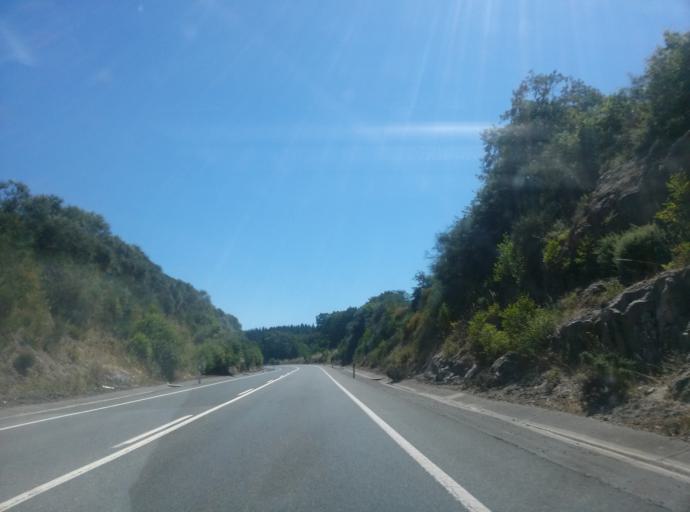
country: ES
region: Galicia
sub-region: Provincia de Lugo
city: Mos
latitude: 43.0946
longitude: -7.4773
